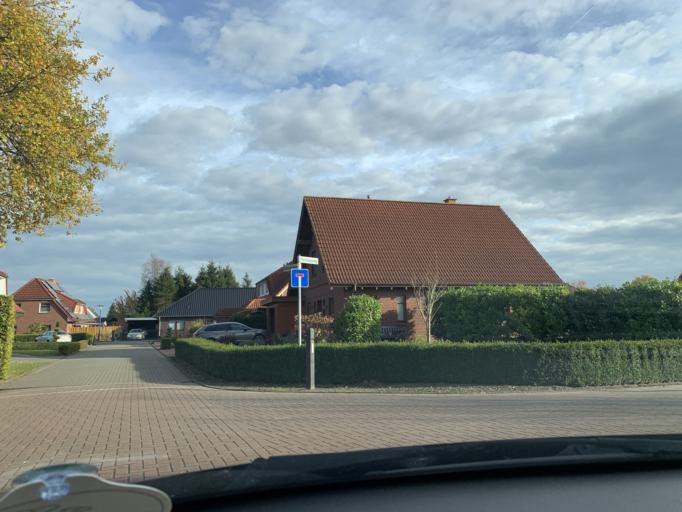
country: DE
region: Lower Saxony
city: Apen
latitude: 53.2186
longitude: 7.8111
